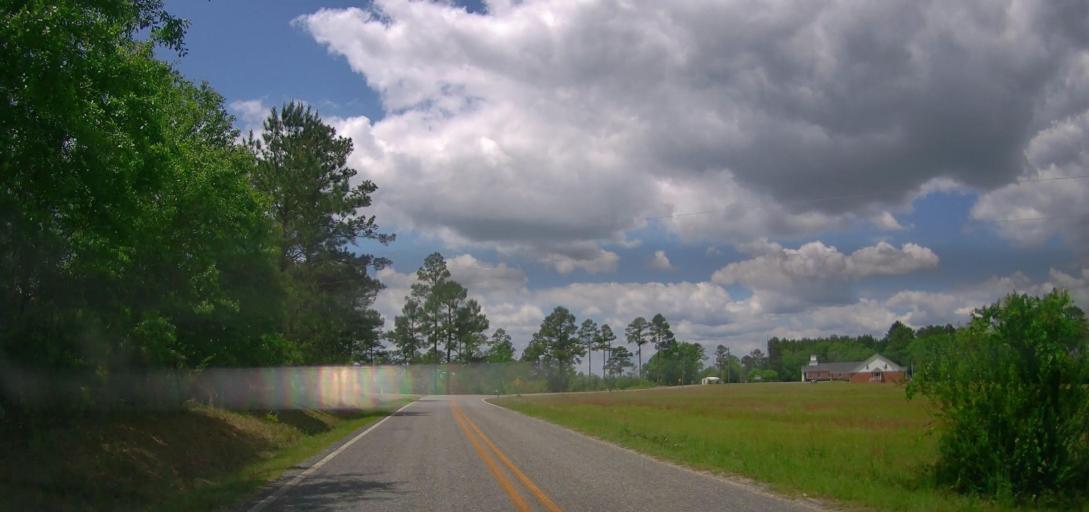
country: US
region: Georgia
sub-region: Laurens County
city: East Dublin
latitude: 32.5884
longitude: -82.7941
